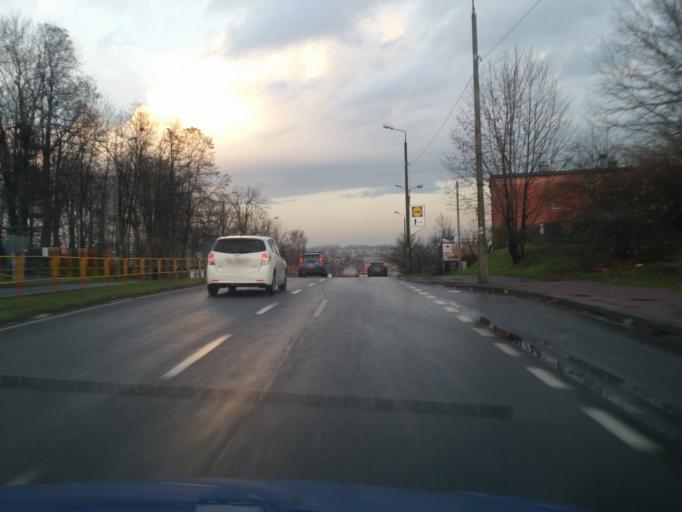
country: PL
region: Silesian Voivodeship
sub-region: Dabrowa Gornicza
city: Dabrowa Gornicza
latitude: 50.2970
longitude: 19.1845
